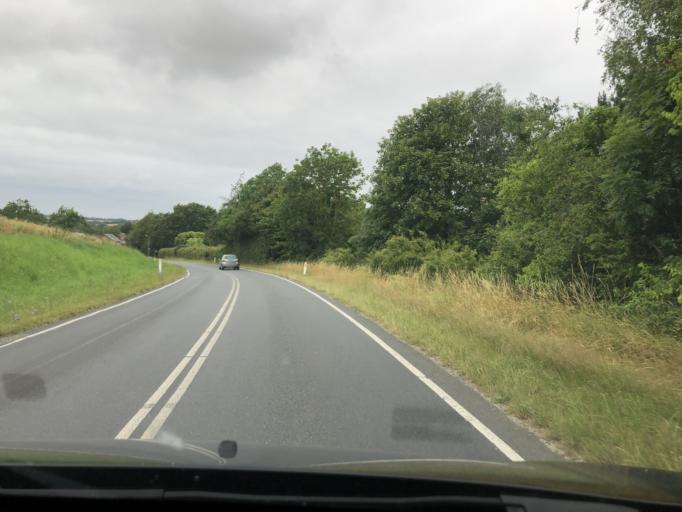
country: DK
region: South Denmark
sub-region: AEro Kommune
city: AEroskobing
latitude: 54.9103
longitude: 10.2894
